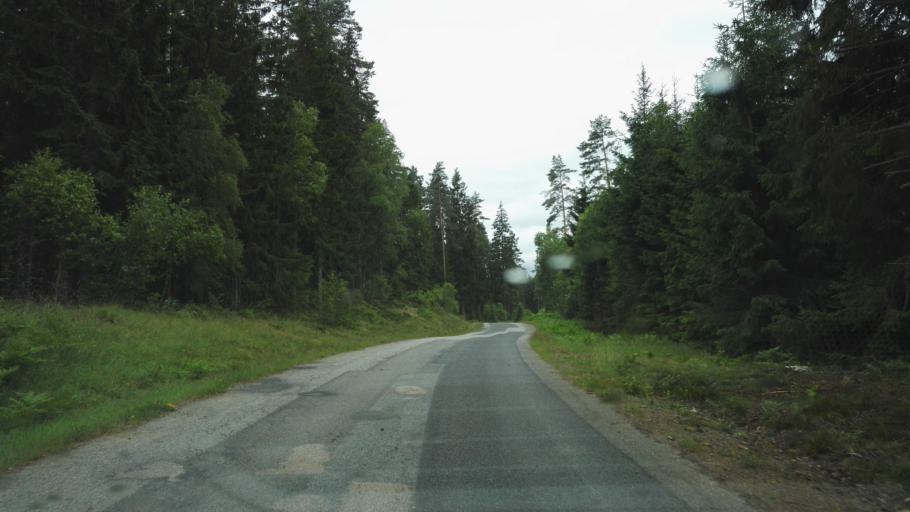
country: SE
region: Joenkoeping
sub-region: Vetlanda Kommun
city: Landsbro
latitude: 57.1974
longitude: 14.7888
